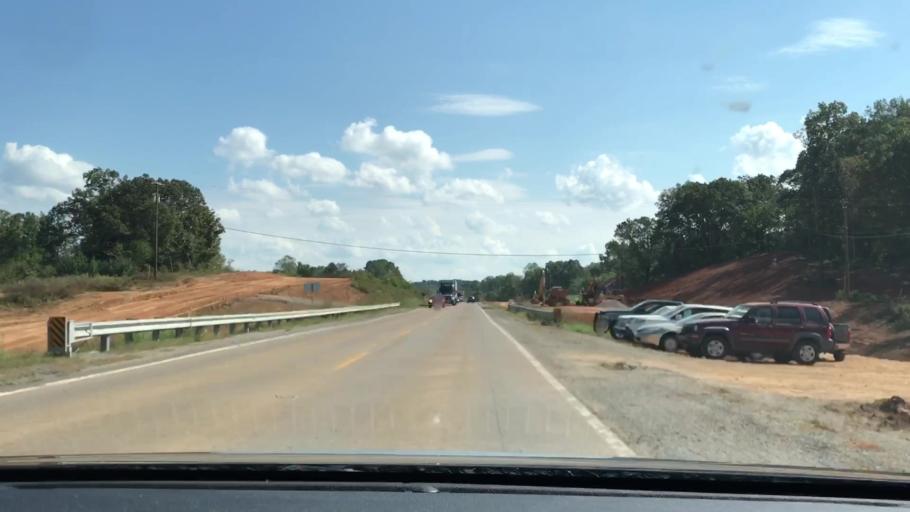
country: US
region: Kentucky
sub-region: Trigg County
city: Cadiz
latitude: 36.7988
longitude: -87.9552
